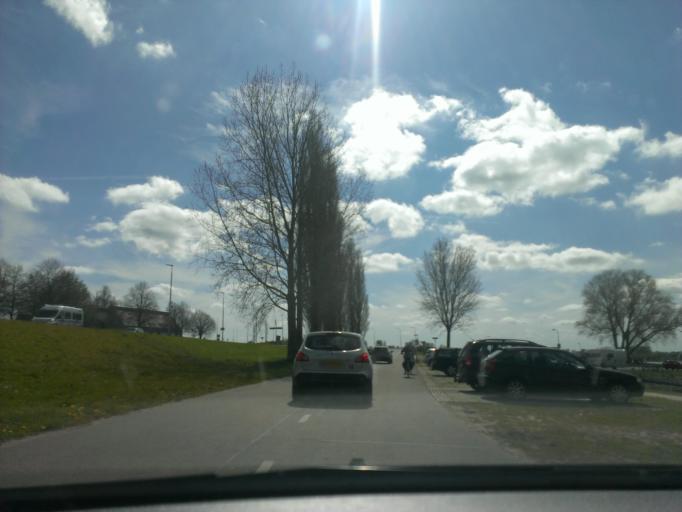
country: NL
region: Overijssel
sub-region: Gemeente Olst-Wijhe
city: Wijhe
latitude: 52.3873
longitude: 6.1286
